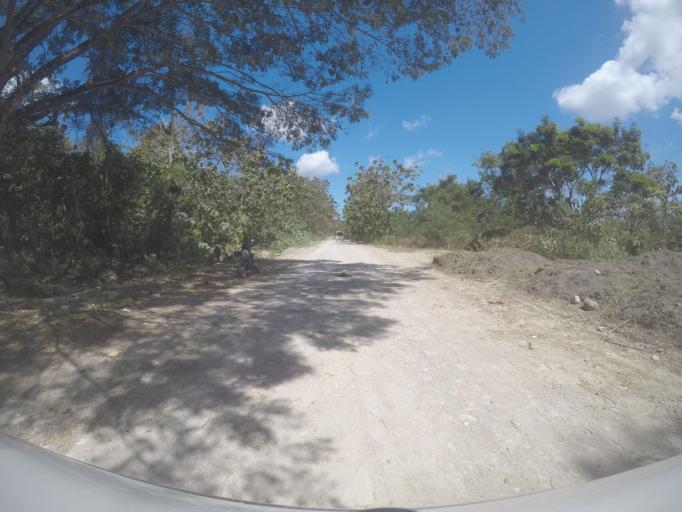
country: TL
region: Viqueque
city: Viqueque
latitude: -8.9092
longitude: 126.3940
